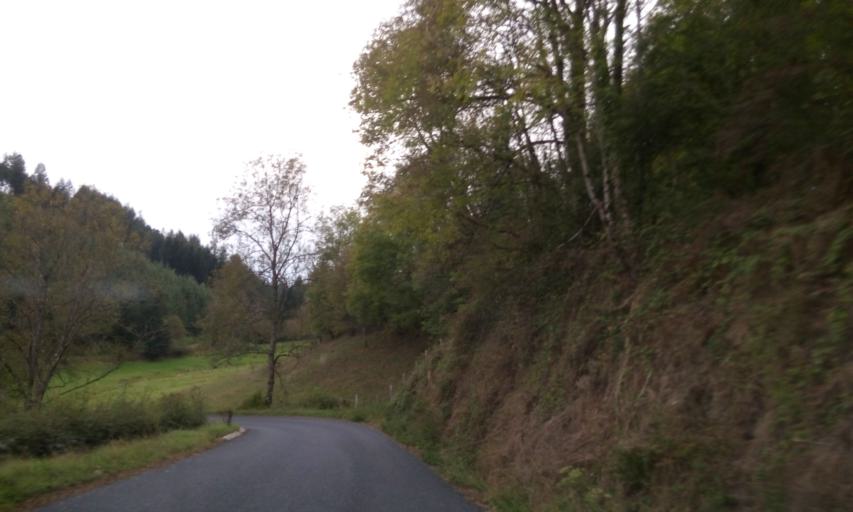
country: FR
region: Rhone-Alpes
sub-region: Departement du Rhone
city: Cublize
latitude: 46.0731
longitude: 4.3904
